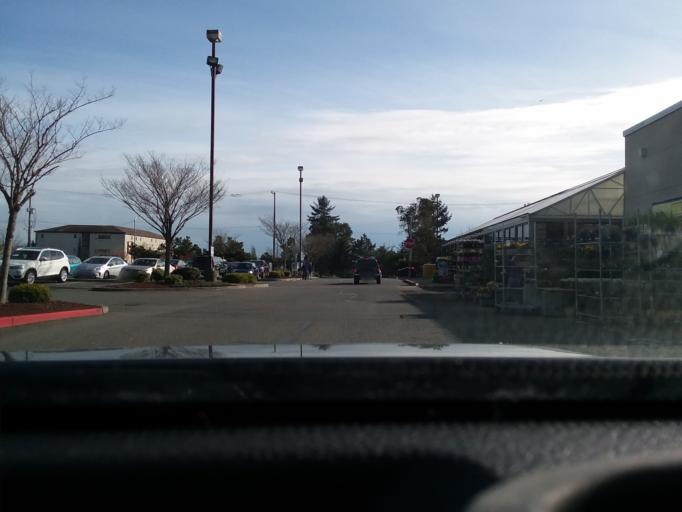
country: US
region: Washington
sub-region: King County
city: Shoreline
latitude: 47.7205
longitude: -122.3466
